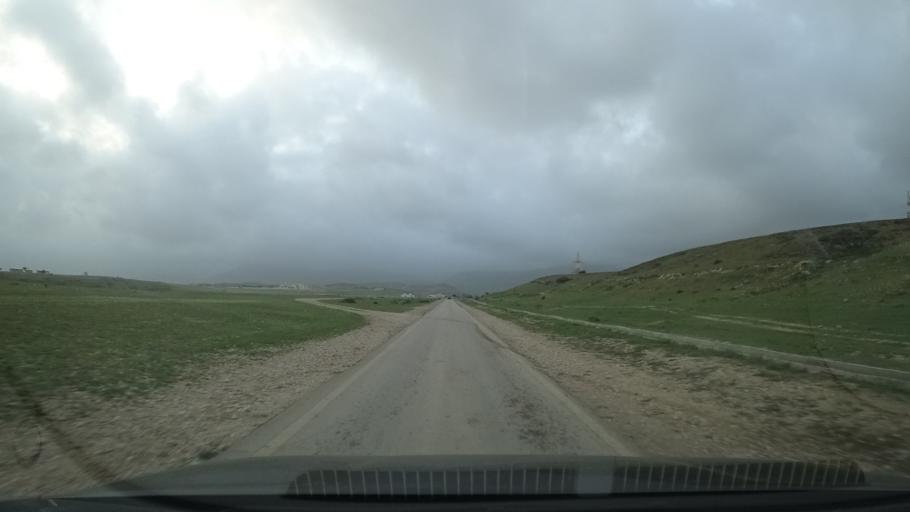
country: OM
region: Zufar
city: Salalah
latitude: 17.1091
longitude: 54.2286
